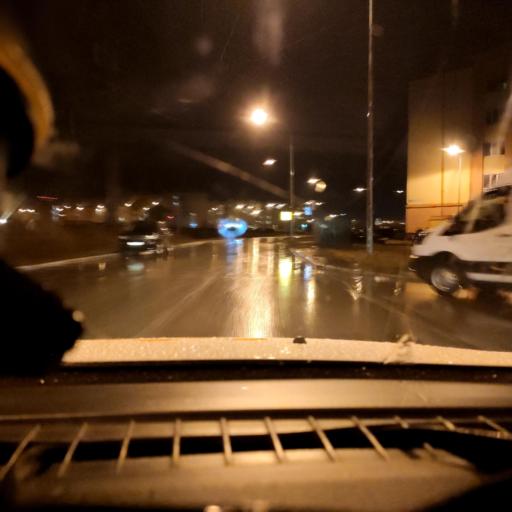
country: RU
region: Samara
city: Samara
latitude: 53.1165
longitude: 50.1515
